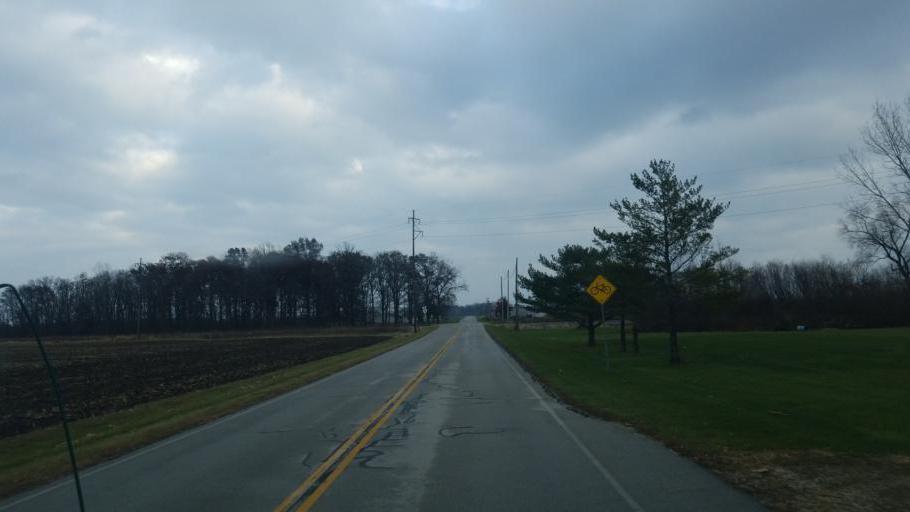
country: US
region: Ohio
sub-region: Mercer County
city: Coldwater
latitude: 40.5091
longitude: -84.6041
